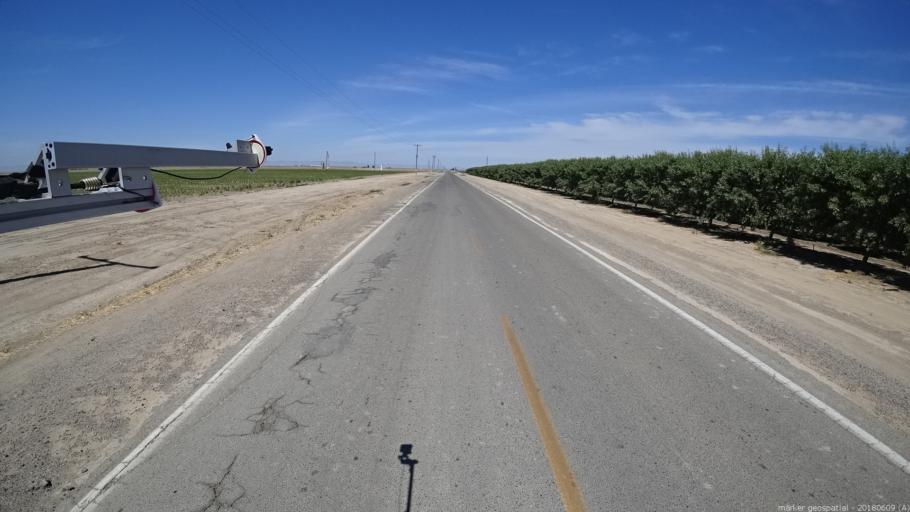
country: US
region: California
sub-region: Fresno County
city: Firebaugh
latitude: 36.9526
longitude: -120.3343
